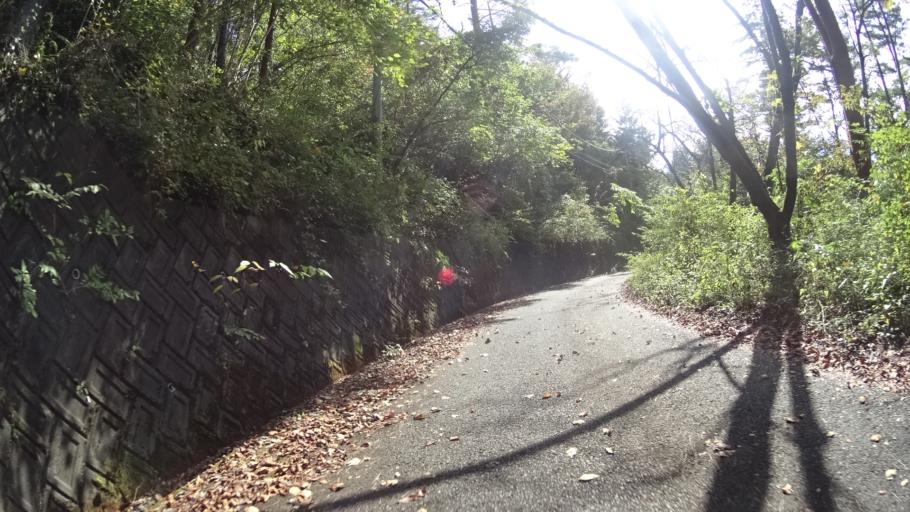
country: JP
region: Yamanashi
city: Otsuki
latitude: 35.5767
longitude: 138.9856
